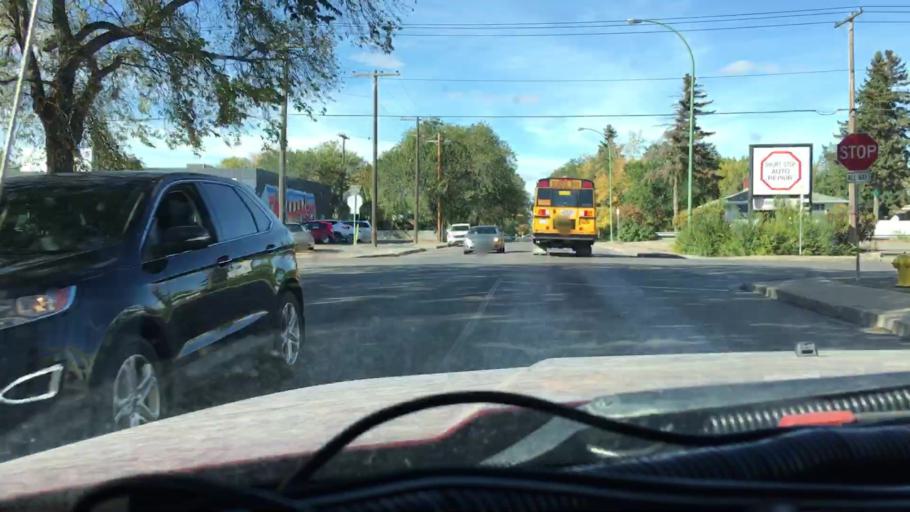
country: CA
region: Saskatchewan
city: Regina
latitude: 50.4611
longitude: -104.6312
